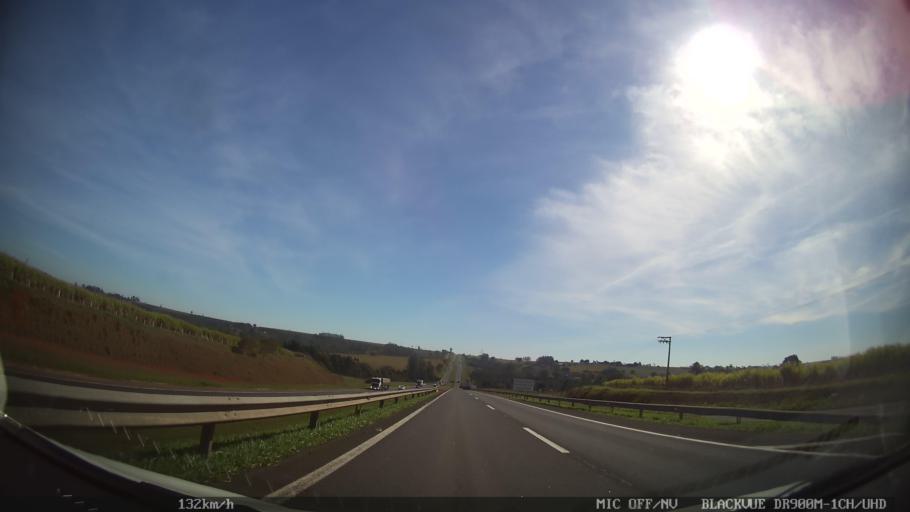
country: BR
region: Sao Paulo
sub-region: Leme
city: Leme
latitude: -22.1049
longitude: -47.4136
